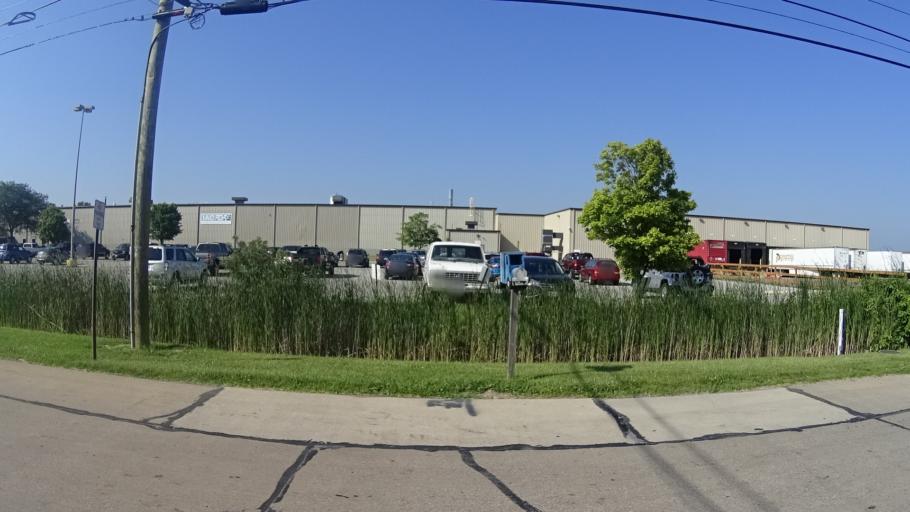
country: US
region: Ohio
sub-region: Erie County
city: Huron
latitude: 41.3990
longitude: -82.5822
